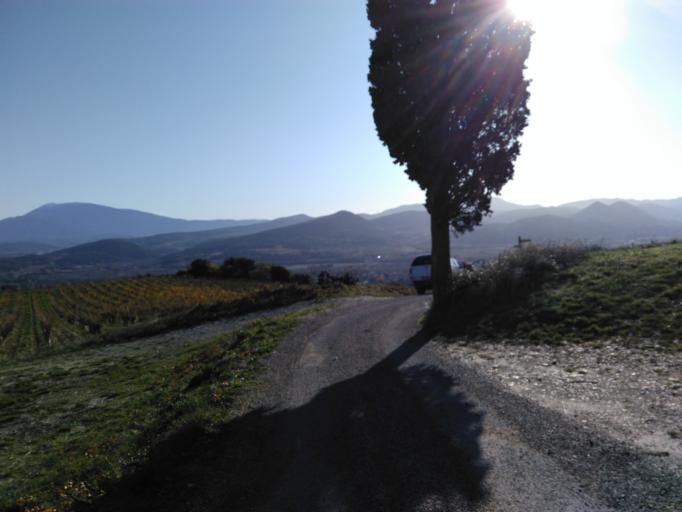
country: FR
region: Provence-Alpes-Cote d'Azur
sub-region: Departement du Vaucluse
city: Sablet
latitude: 44.2583
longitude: 5.0085
